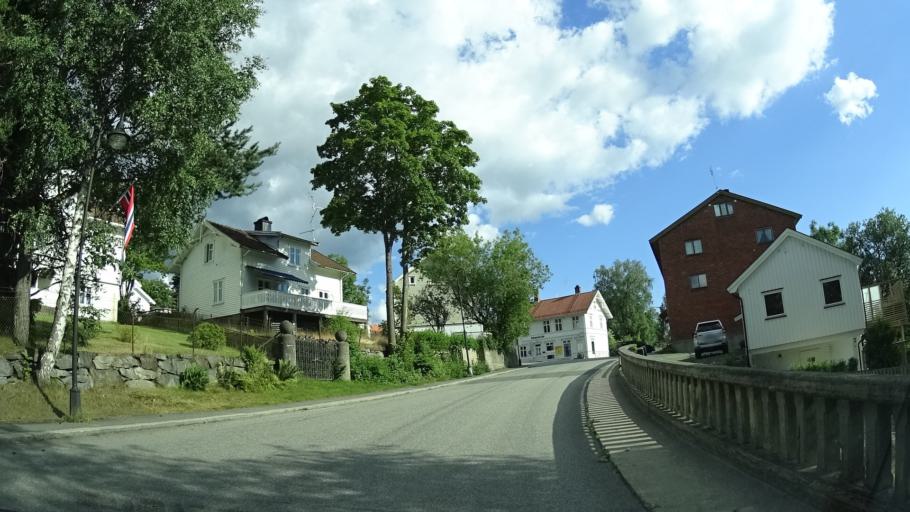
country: NO
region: Ostfold
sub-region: Marker
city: Orje
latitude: 59.4820
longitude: 11.6541
